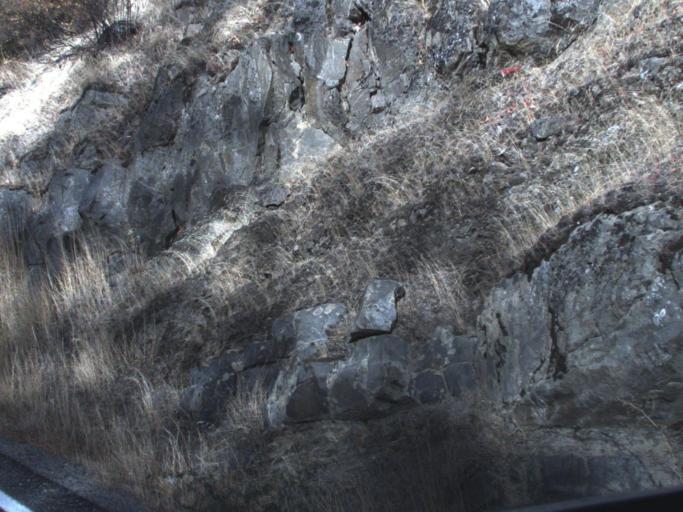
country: US
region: Washington
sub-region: Stevens County
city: Kettle Falls
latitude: 48.3380
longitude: -118.1575
